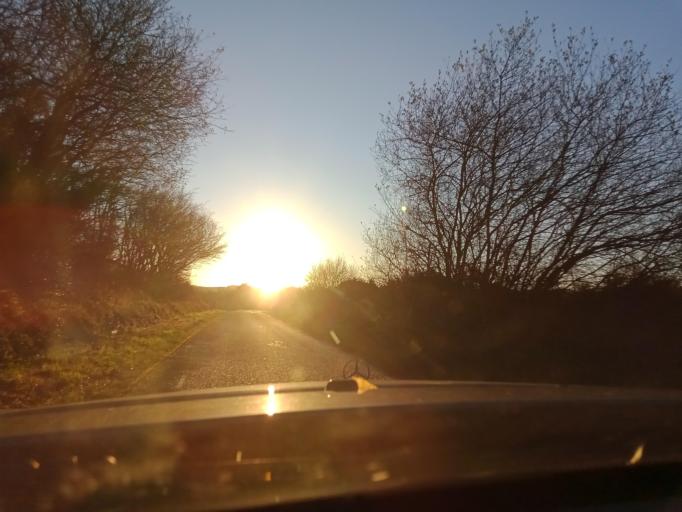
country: IE
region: Munster
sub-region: Waterford
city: Waterford
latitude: 52.3678
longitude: -7.1134
